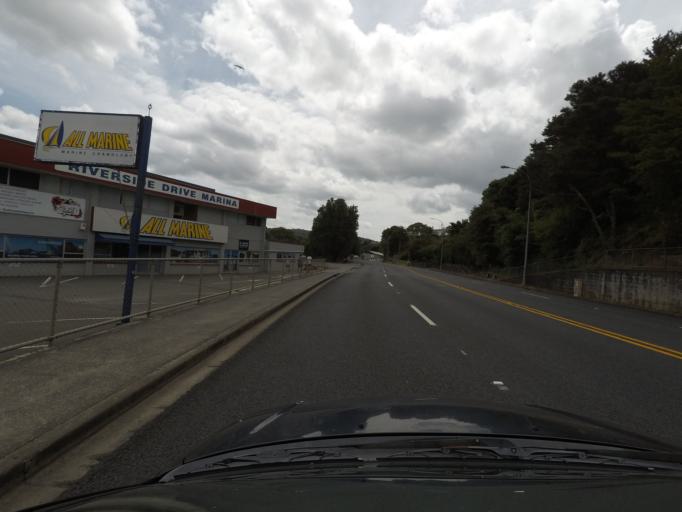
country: NZ
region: Northland
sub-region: Whangarei
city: Whangarei
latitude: -35.7272
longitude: 174.3338
